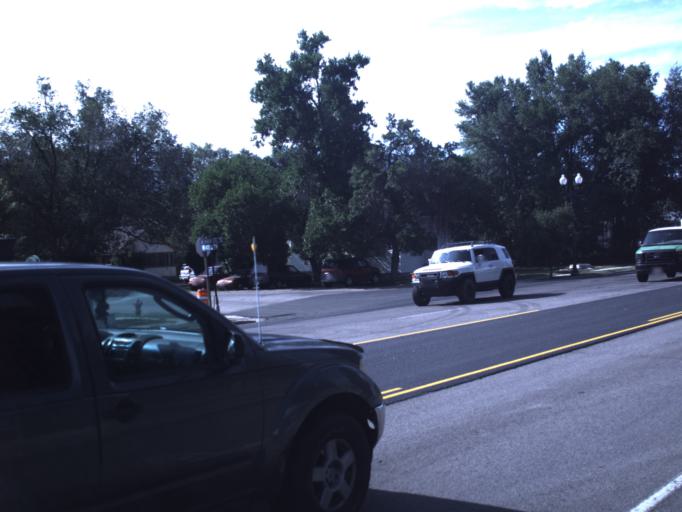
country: US
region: Utah
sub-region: Wasatch County
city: Heber
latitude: 40.5023
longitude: -111.4134
